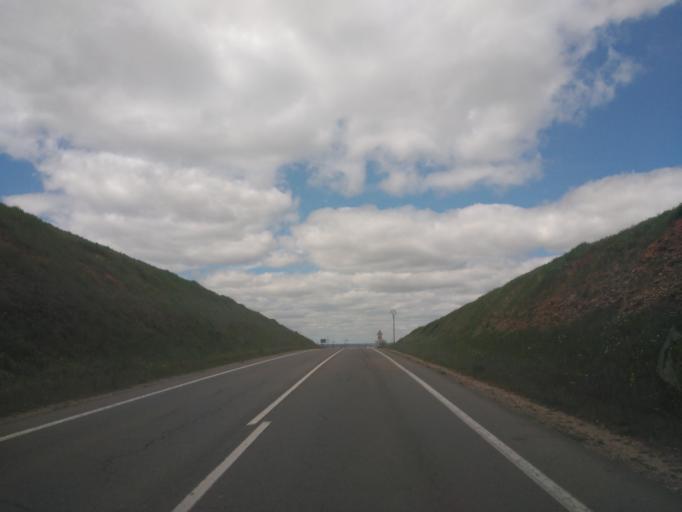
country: ES
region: Castille and Leon
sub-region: Provincia de Salamanca
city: Villamayor
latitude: 40.9834
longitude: -5.6807
